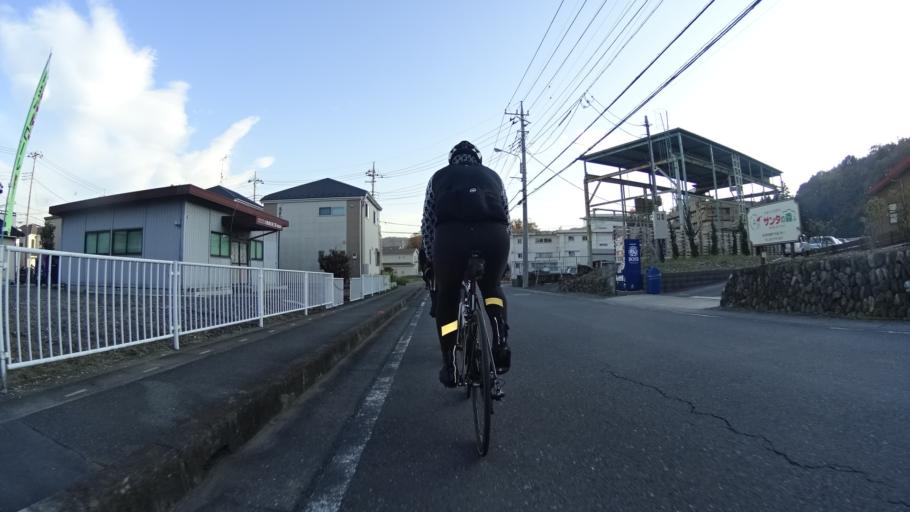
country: JP
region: Saitama
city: Hanno
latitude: 35.8417
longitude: 139.3181
